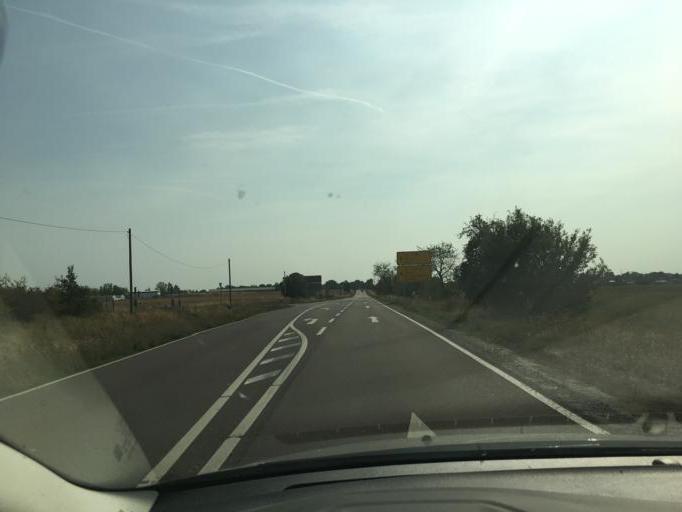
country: DE
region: Saxony-Anhalt
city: Nienburg/Saale
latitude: 51.8162
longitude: 11.8092
